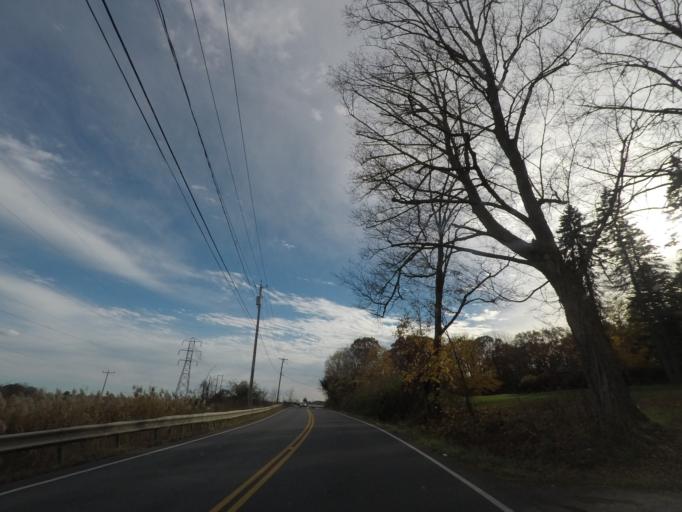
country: US
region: New York
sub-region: Albany County
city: Voorheesville
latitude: 42.6165
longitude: -73.9077
